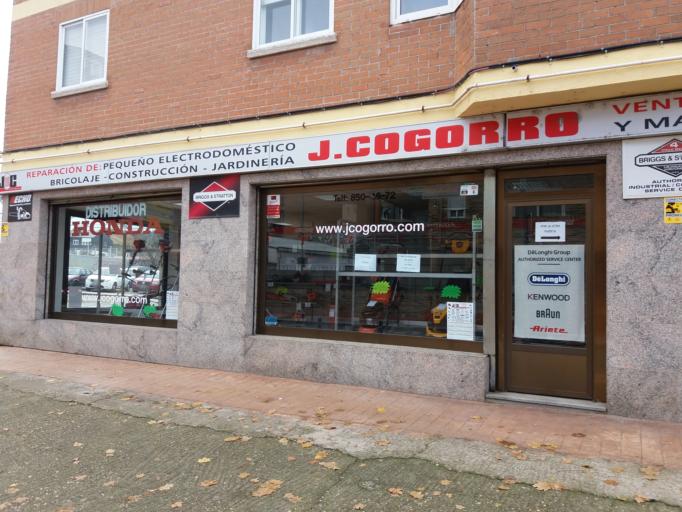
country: ES
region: Madrid
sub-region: Provincia de Madrid
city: Collado-Villalba
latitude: 40.6279
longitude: -4.0141
